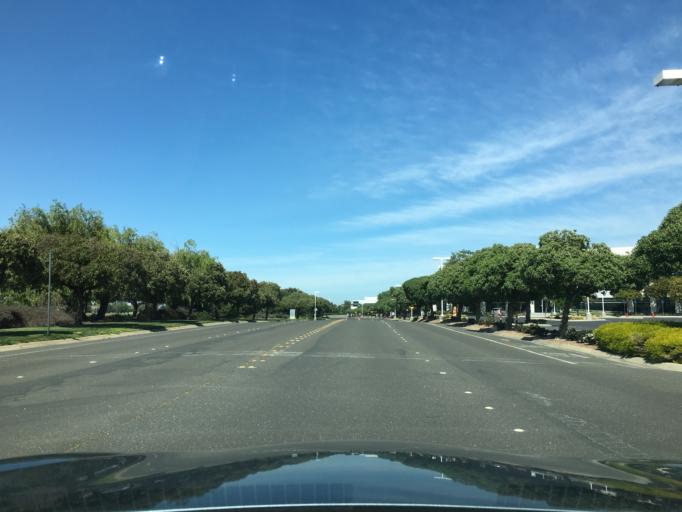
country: US
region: California
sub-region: San Mateo County
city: Redwood Shores
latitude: 37.5322
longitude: -122.2595
